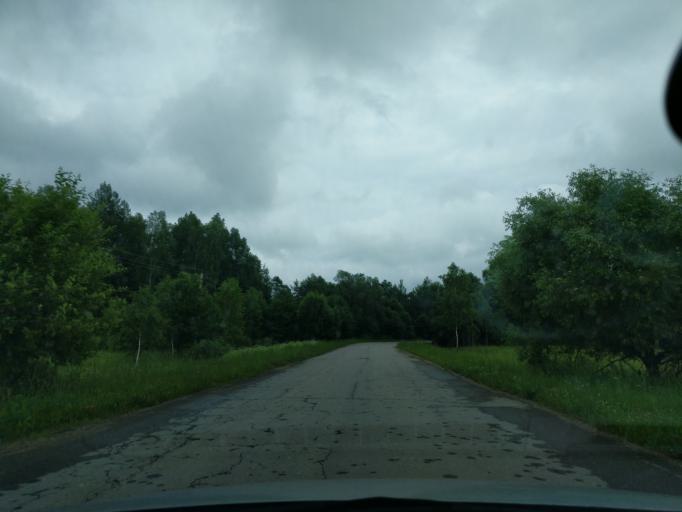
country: RU
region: Kaluga
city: Myatlevo
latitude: 54.8398
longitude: 35.6318
